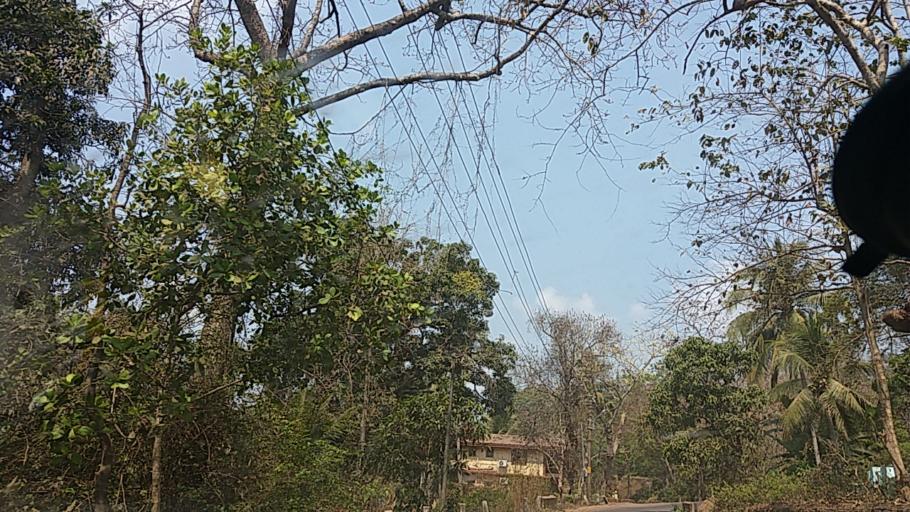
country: IN
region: Goa
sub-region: South Goa
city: Sancoale
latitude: 15.3743
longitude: 73.9143
